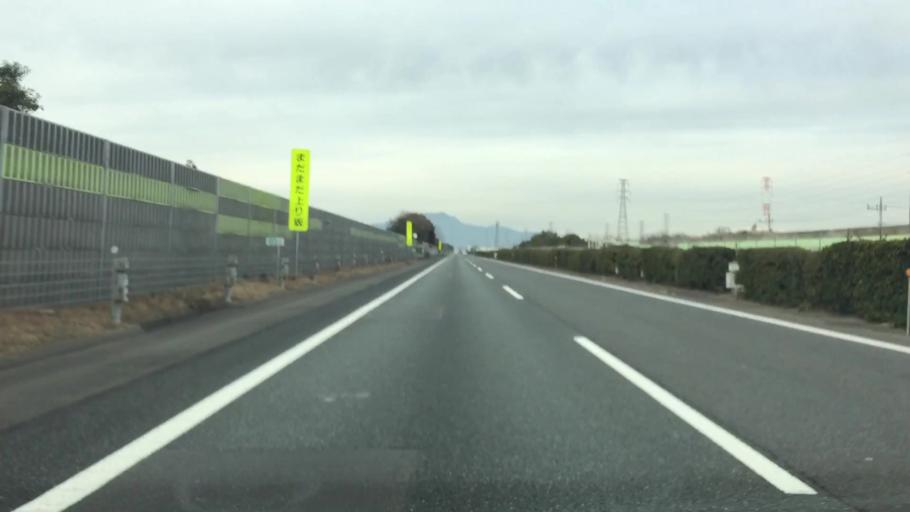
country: JP
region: Gunma
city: Maebashi-shi
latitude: 36.3866
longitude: 139.0262
